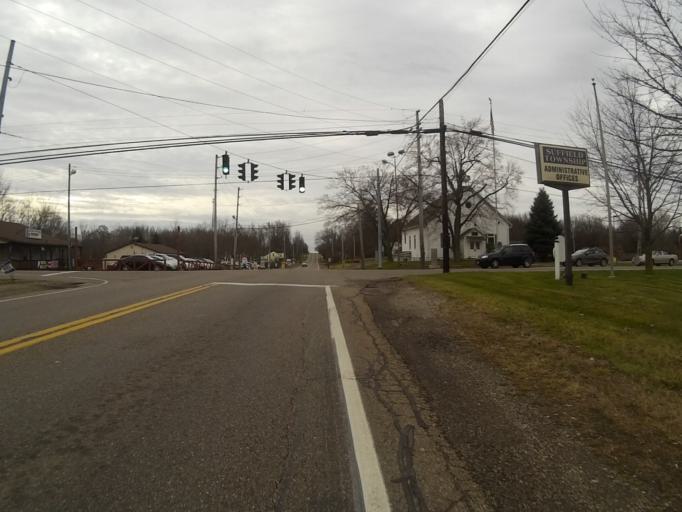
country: US
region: Ohio
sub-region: Summit County
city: Mogadore
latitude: 41.0235
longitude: -81.3474
